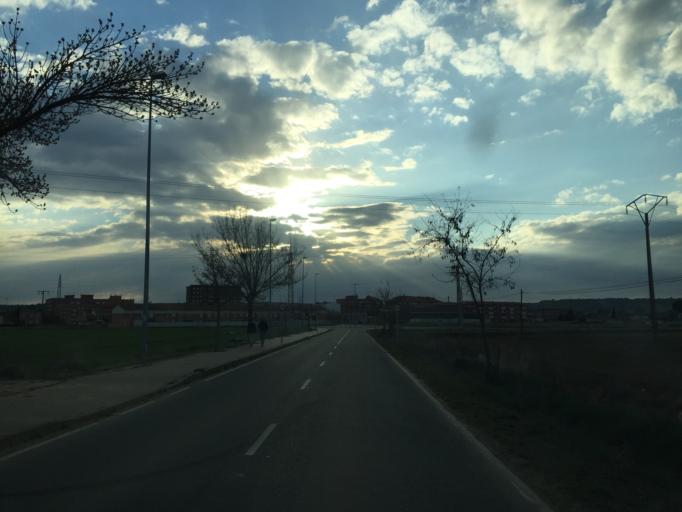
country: ES
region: Castille and Leon
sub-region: Provincia de Palencia
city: Venta de Banos
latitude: 41.9214
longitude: -4.4835
